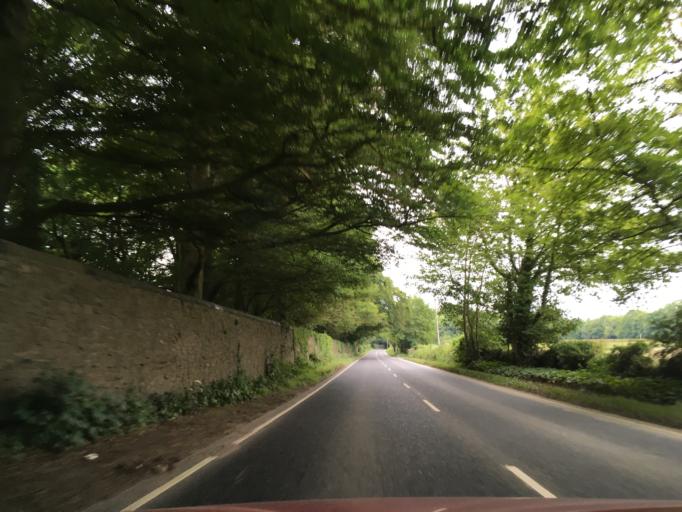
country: GB
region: England
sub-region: North Somerset
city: Long Ashton
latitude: 51.4481
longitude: -2.6585
